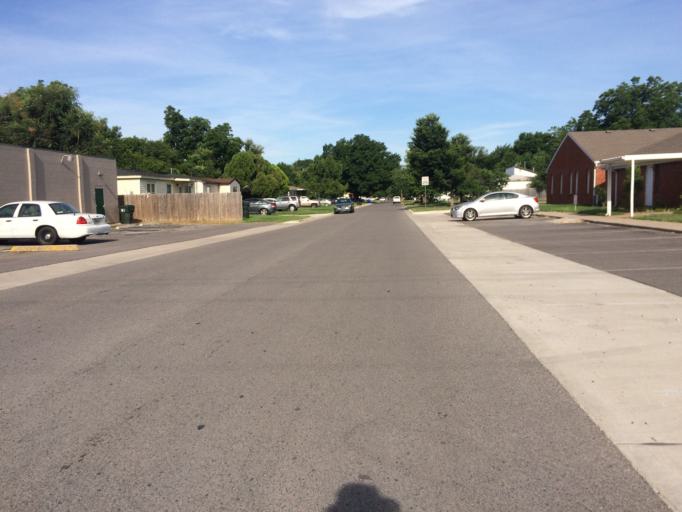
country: US
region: Oklahoma
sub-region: Cleveland County
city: Norman
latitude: 35.2244
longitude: -97.4592
